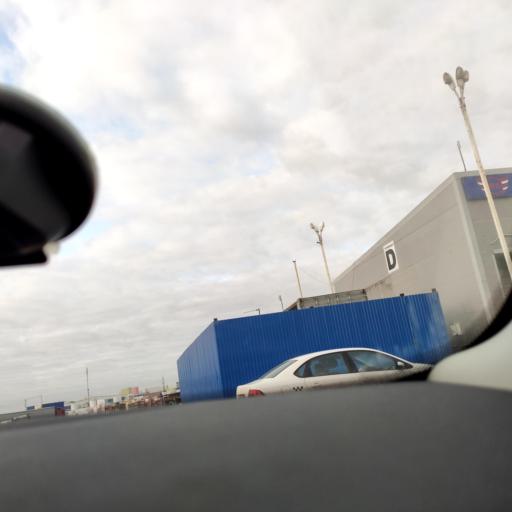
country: RU
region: Moskovskaya
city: Mosrentgen
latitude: 55.6216
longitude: 37.4551
